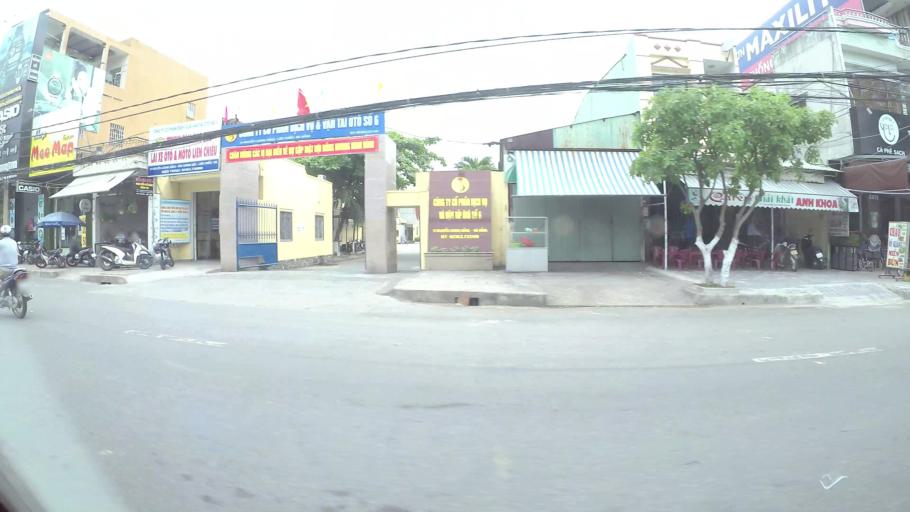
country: VN
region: Da Nang
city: Lien Chieu
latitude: 16.0740
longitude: 108.1494
